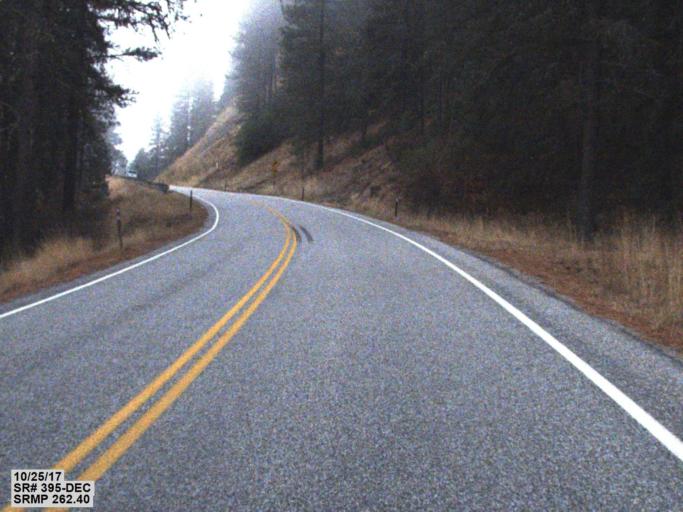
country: CA
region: British Columbia
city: Grand Forks
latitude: 48.8952
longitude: -118.2189
